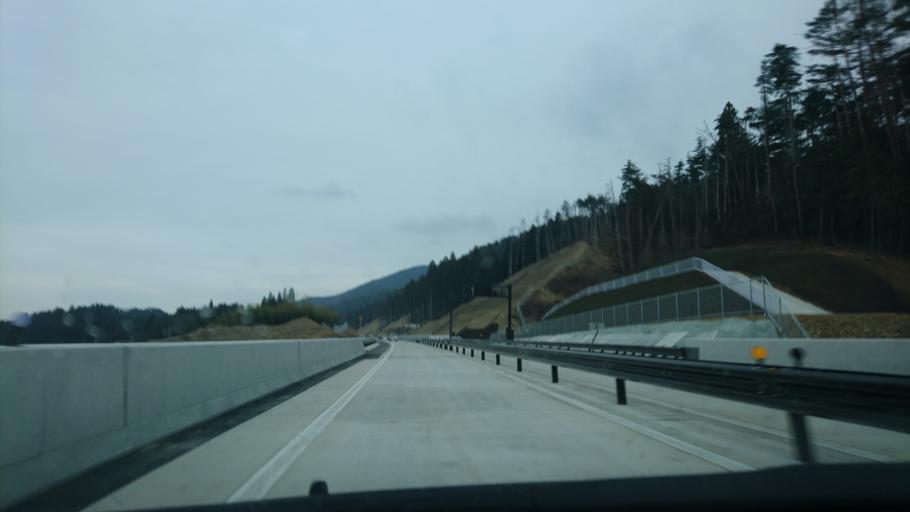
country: JP
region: Iwate
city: Ofunato
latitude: 38.9640
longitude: 141.6243
